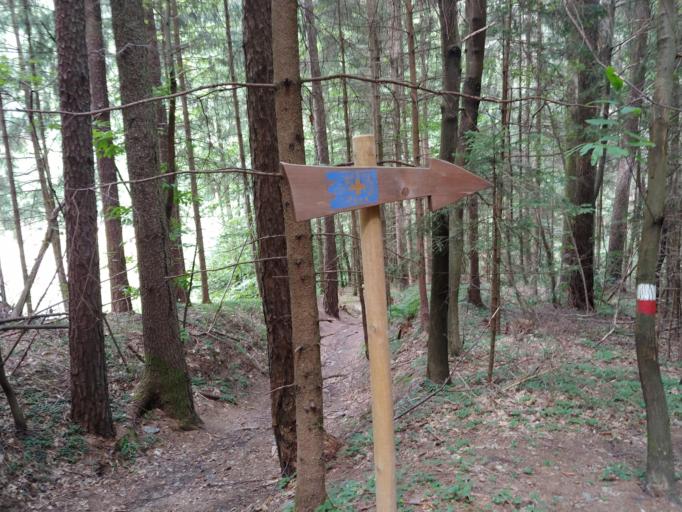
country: IT
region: Trentino-Alto Adige
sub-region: Bolzano
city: Bressanone
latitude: 46.7144
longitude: 11.6370
